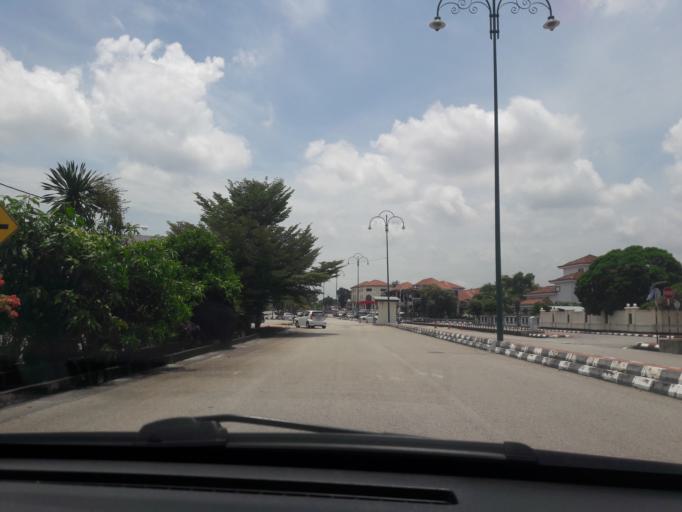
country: MY
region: Kedah
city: Sungai Petani
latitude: 5.6605
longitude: 100.4993
